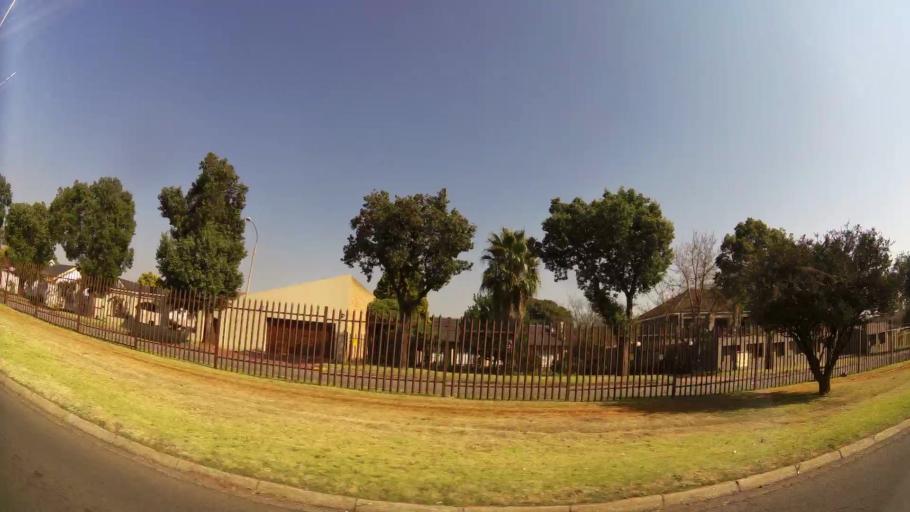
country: ZA
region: Gauteng
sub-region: Ekurhuleni Metropolitan Municipality
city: Boksburg
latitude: -26.2445
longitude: 28.2630
